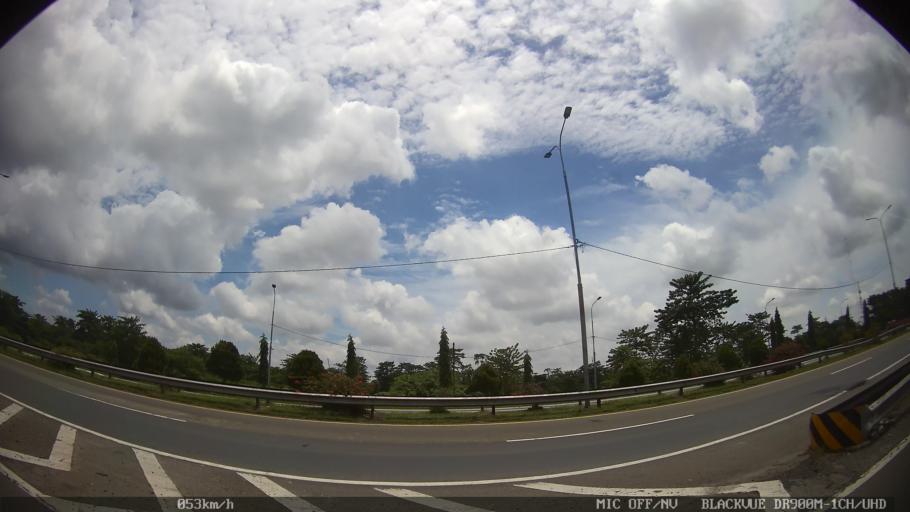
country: ID
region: North Sumatra
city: Medan
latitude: 3.6008
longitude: 98.7235
